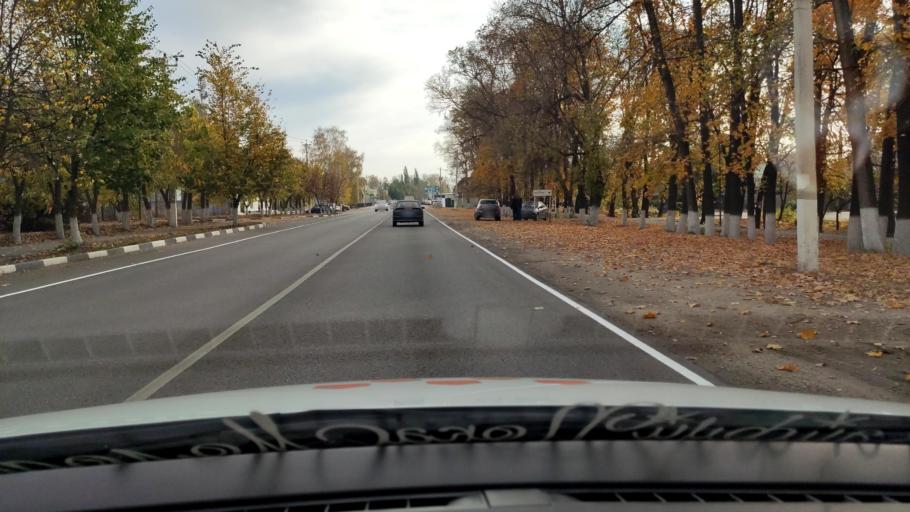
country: RU
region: Voronezj
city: Ramon'
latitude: 51.9108
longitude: 39.3290
